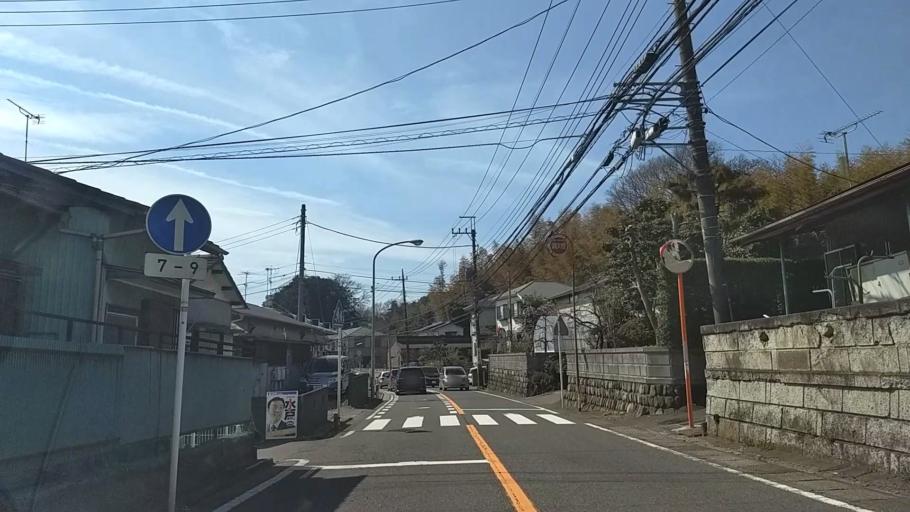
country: JP
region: Kanagawa
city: Fujisawa
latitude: 35.3876
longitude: 139.5064
